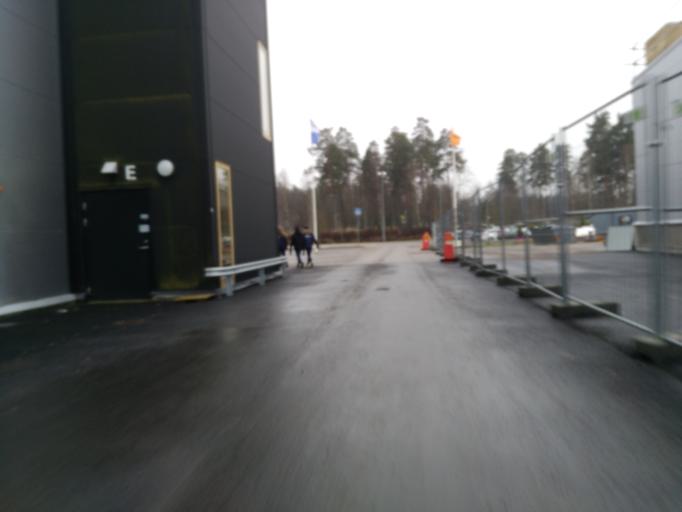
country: SE
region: Vaestra Goetaland
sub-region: Lidkopings Kommun
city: Lidkoping
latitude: 58.4945
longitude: 13.1416
